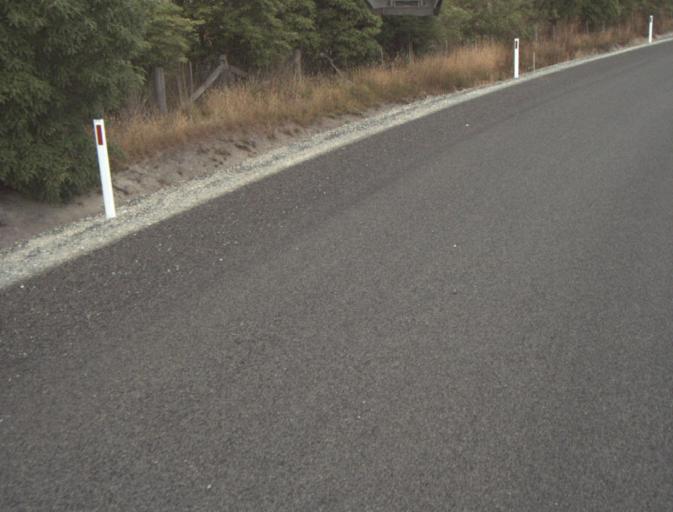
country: AU
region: Tasmania
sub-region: Launceston
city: Mayfield
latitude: -41.2002
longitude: 147.1896
